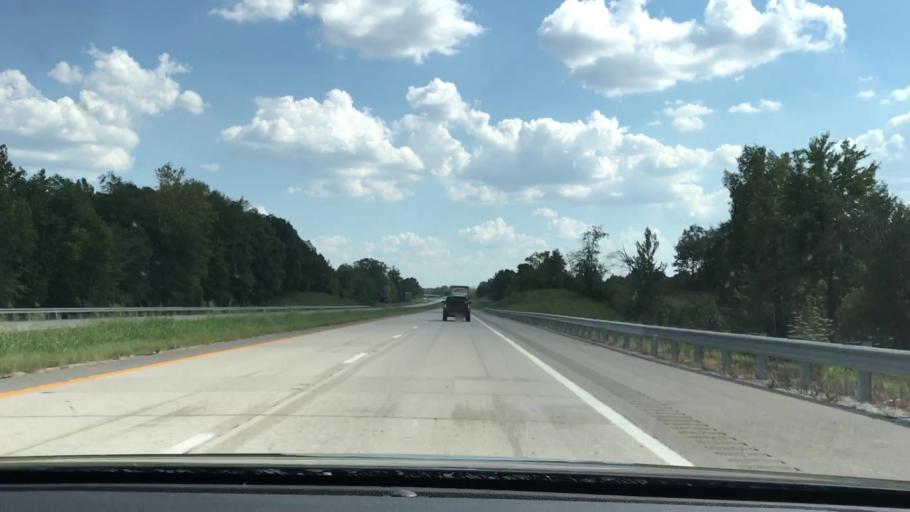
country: US
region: Kentucky
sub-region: Ohio County
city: Oak Grove
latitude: 37.3626
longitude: -86.7950
